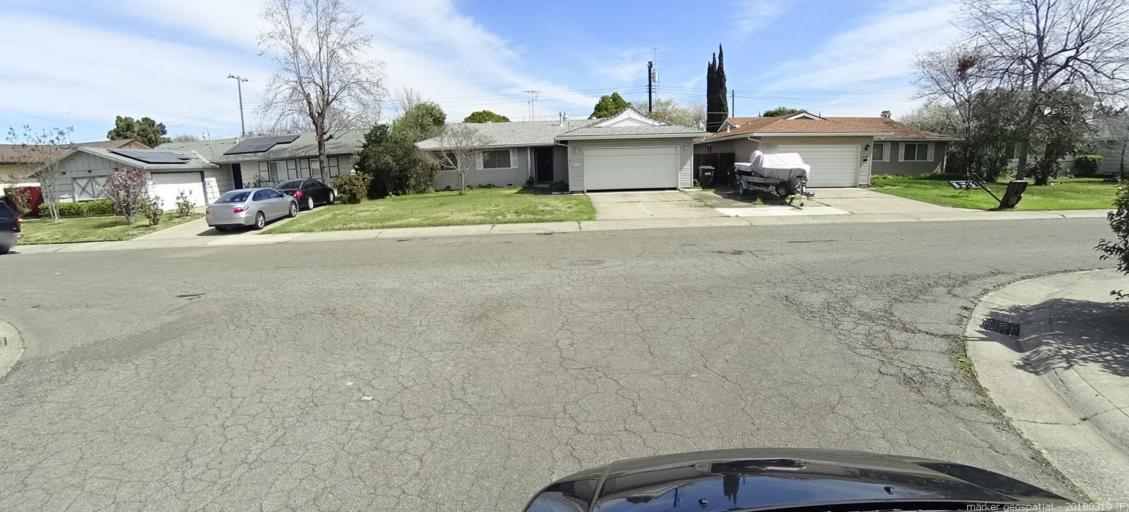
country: US
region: California
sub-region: Sacramento County
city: Parkway
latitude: 38.5055
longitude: -121.4486
